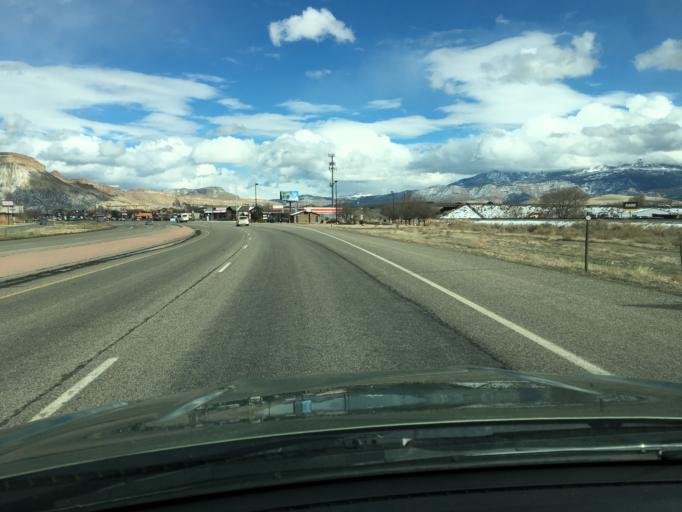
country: US
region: Colorado
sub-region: Mesa County
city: Clifton
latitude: 39.0856
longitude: -108.4618
